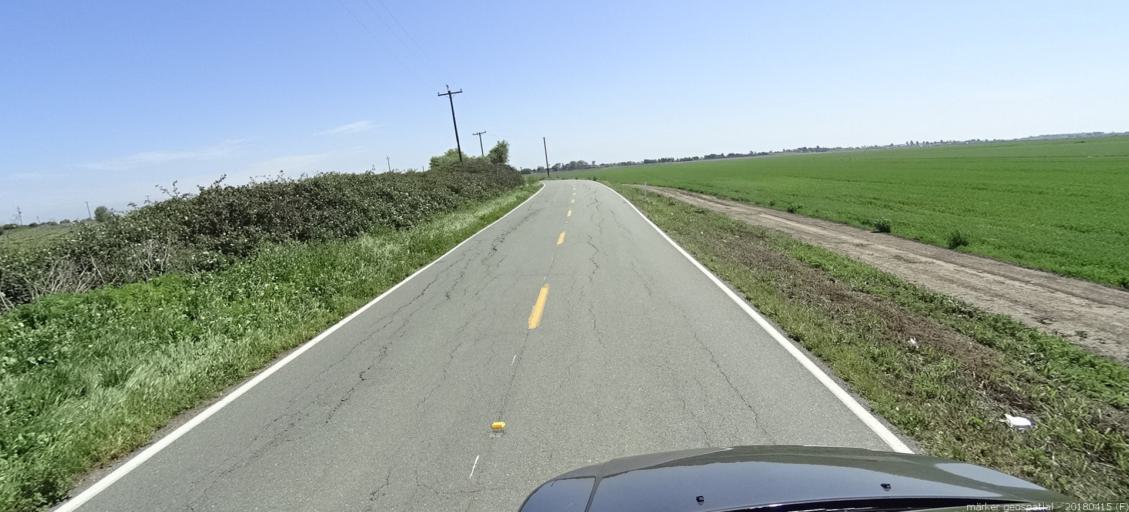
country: US
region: California
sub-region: Solano County
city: Rio Vista
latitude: 38.1451
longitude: -121.6195
